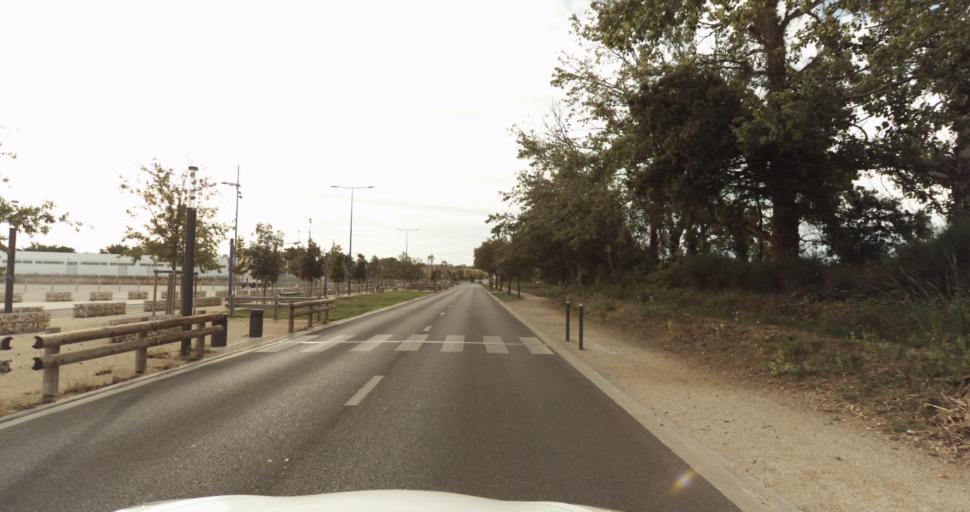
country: FR
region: Provence-Alpes-Cote d'Azur
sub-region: Departement des Bouches-du-Rhone
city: Miramas
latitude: 43.5932
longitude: 4.9990
